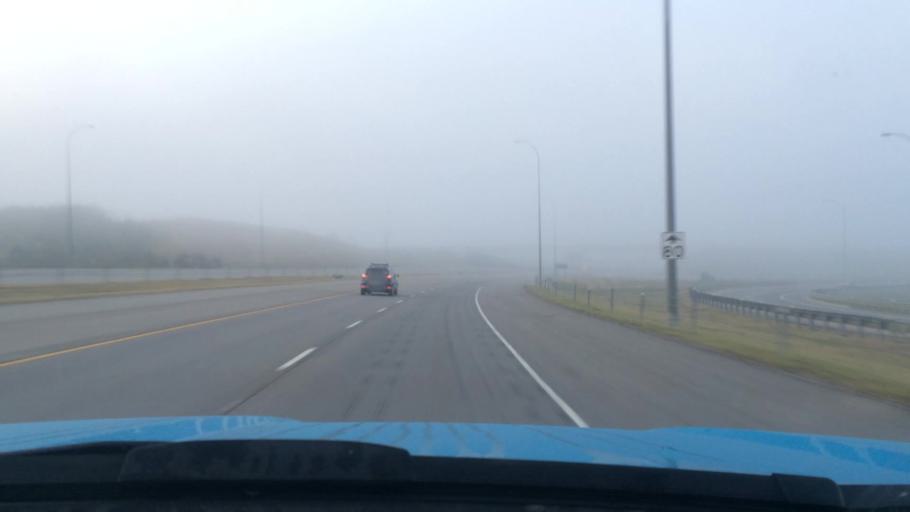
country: CA
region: Alberta
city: Calgary
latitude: 51.1100
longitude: -114.2246
